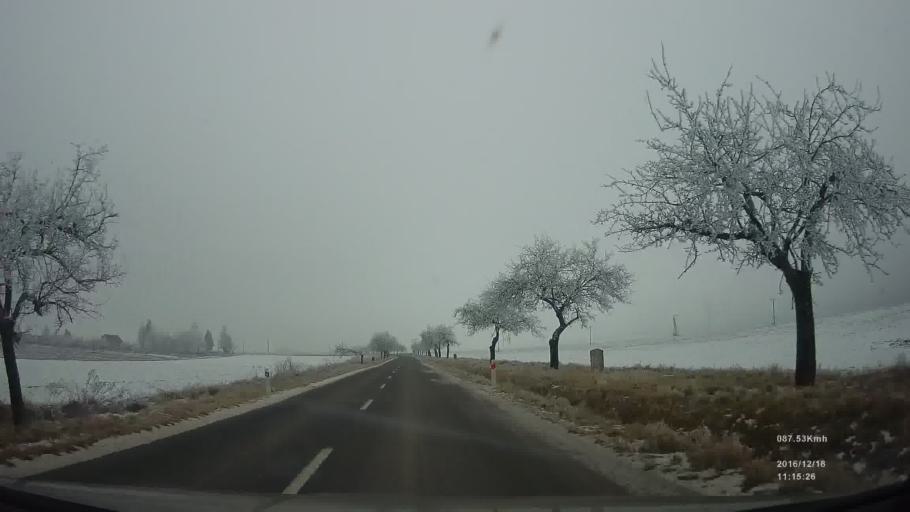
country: SK
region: Presovsky
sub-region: Okres Presov
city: Presov
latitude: 48.9051
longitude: 21.3239
